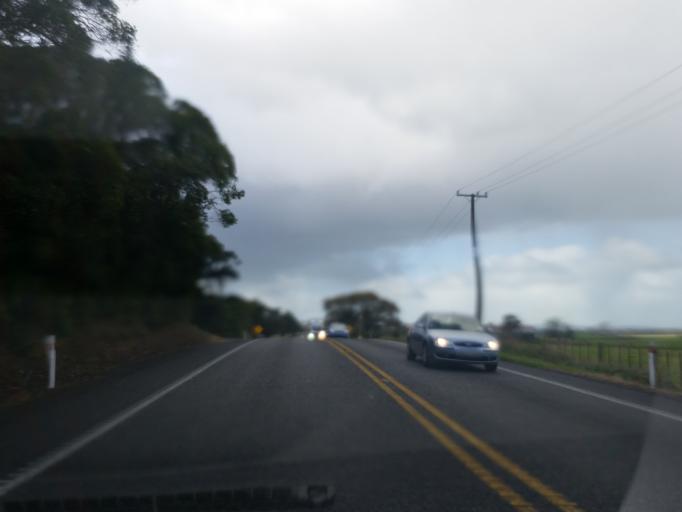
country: NZ
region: Auckland
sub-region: Auckland
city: Pukekohe East
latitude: -37.2160
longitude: 175.0591
